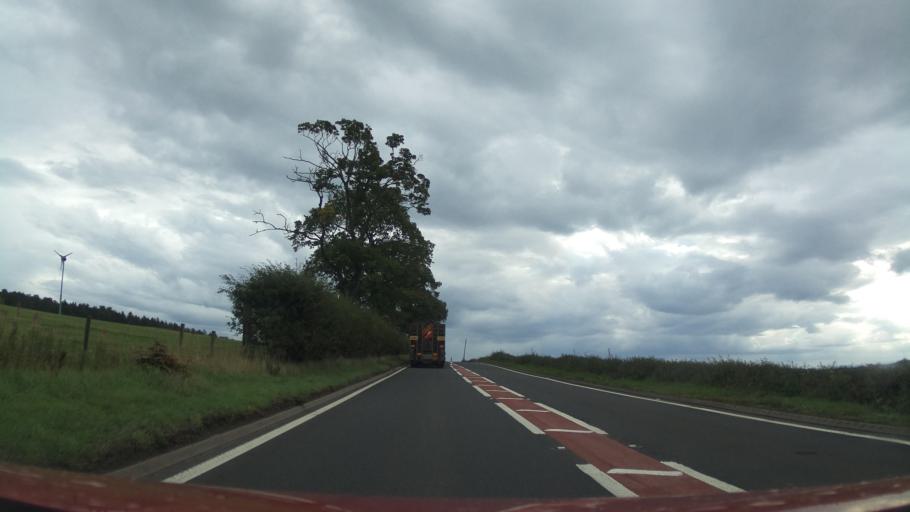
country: GB
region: Scotland
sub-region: Fife
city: Kincardine
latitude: 56.0644
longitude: -3.6871
